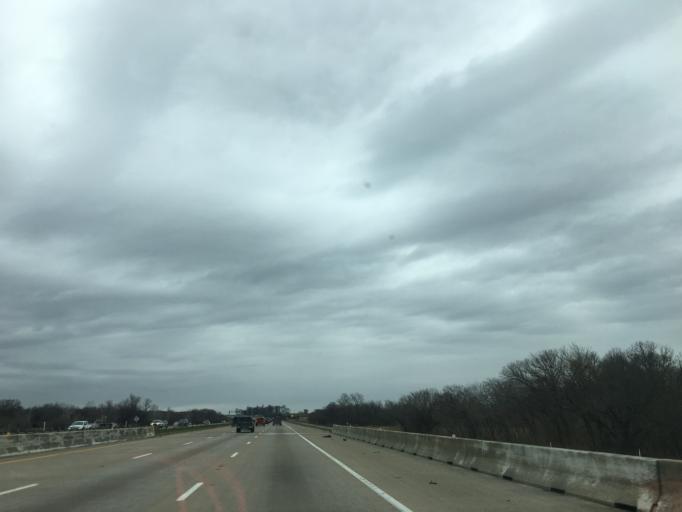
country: US
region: Texas
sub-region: Ellis County
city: Palmer
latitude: 32.4615
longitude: -96.6625
